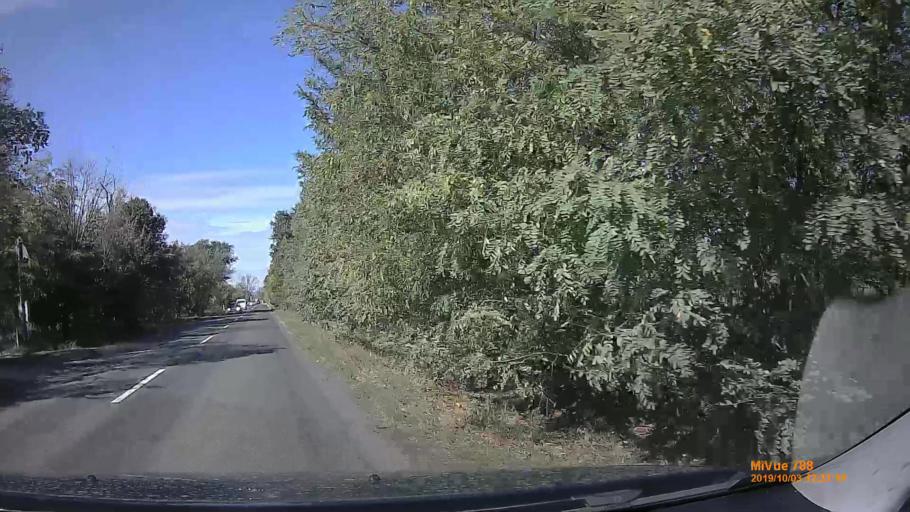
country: HU
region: Pest
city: Szodliget
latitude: 47.7540
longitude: 19.1617
